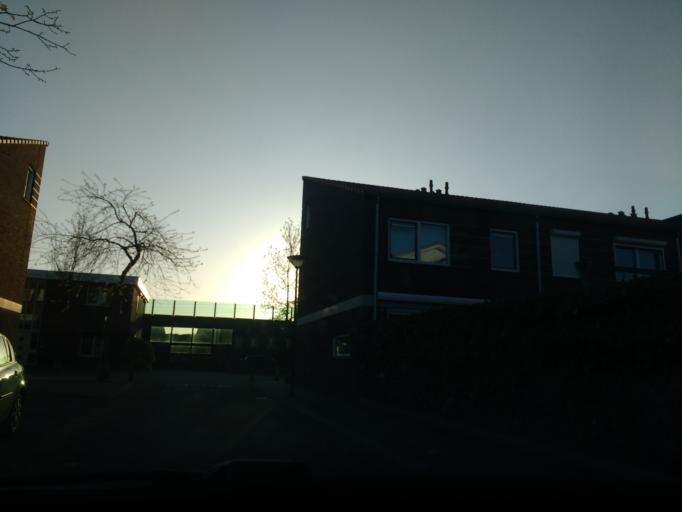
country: NL
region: Gelderland
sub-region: Gemeente Overbetuwe
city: Elst
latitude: 51.9216
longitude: 5.8558
